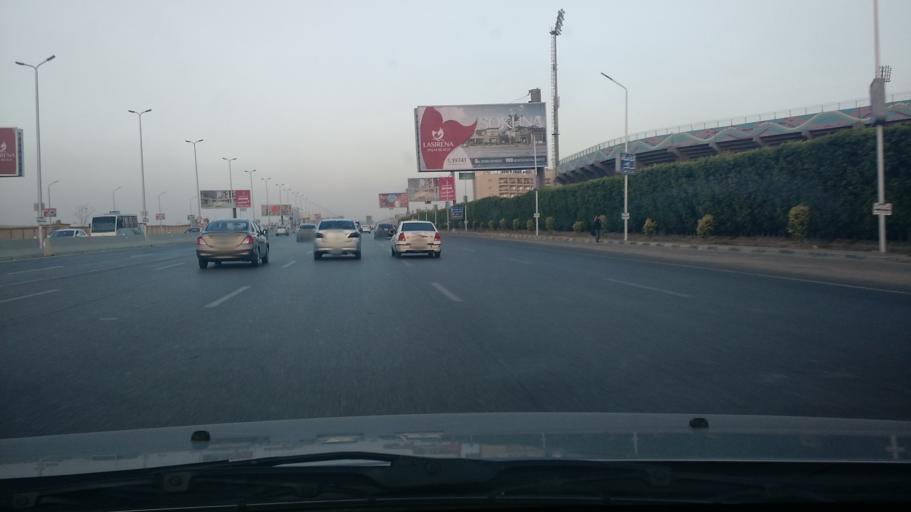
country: EG
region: Muhafazat al Qahirah
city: Cairo
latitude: 30.0218
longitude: 31.3725
